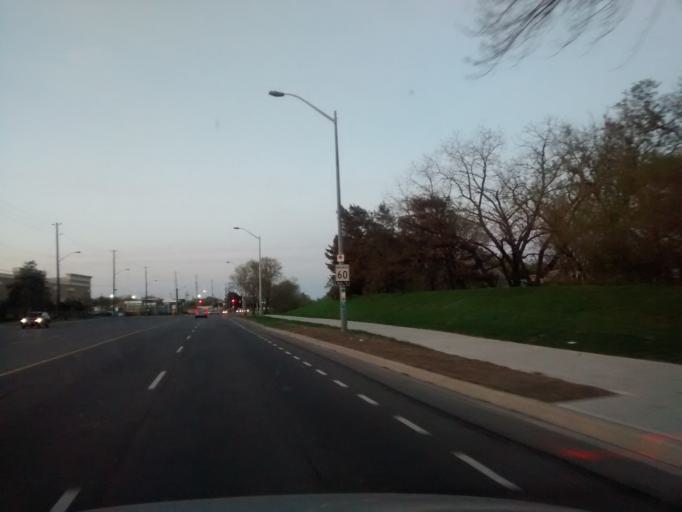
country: CA
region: Ontario
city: Burlington
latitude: 43.3364
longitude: -79.8119
